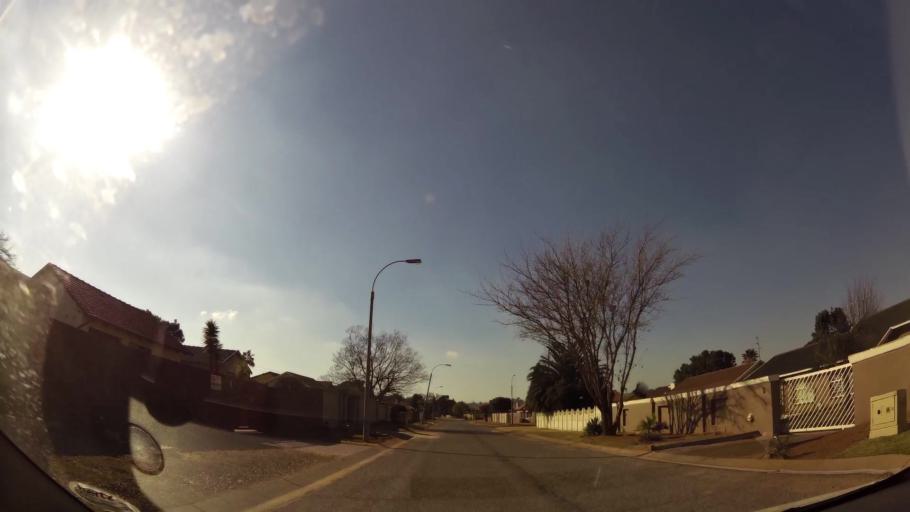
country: ZA
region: Gauteng
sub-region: City of Johannesburg Metropolitan Municipality
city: Roodepoort
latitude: -26.1664
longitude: 27.8288
